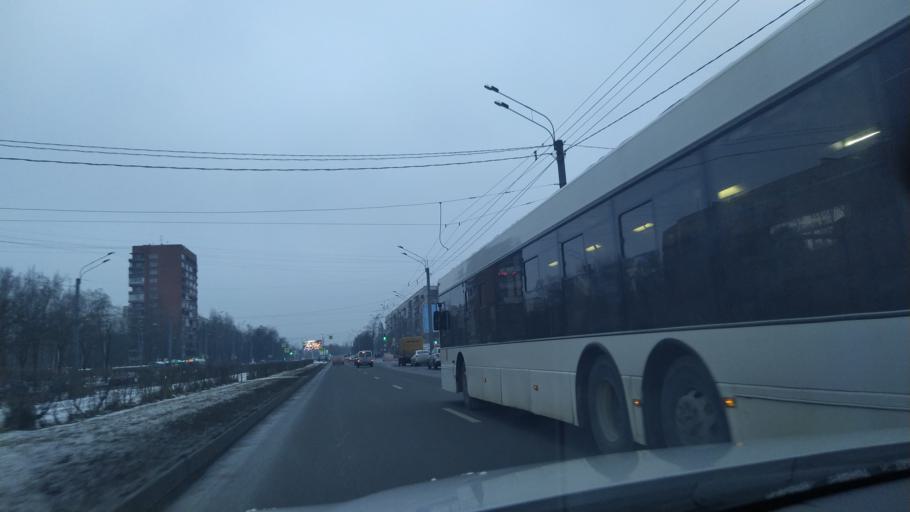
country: RU
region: St.-Petersburg
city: Grazhdanka
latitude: 60.0357
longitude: 30.3954
